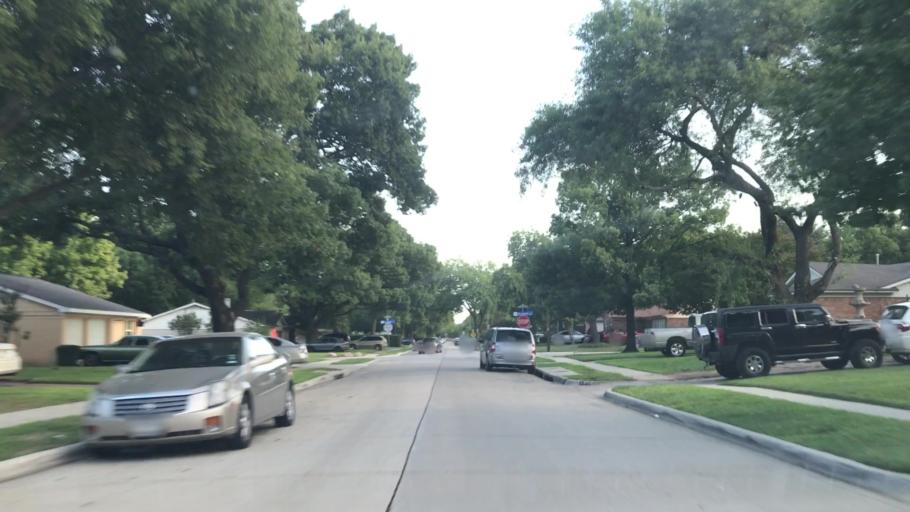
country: US
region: Texas
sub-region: Dallas County
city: Richardson
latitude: 32.9483
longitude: -96.7585
